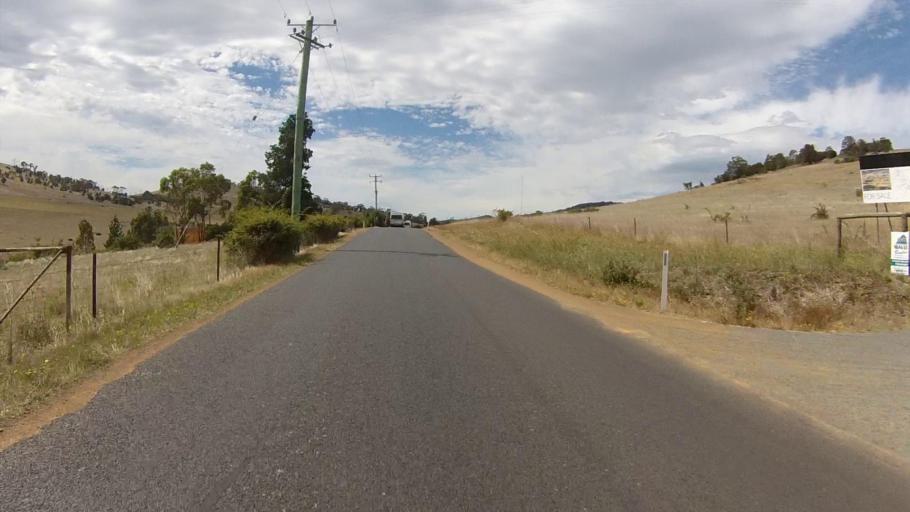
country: AU
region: Tasmania
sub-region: Brighton
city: Old Beach
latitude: -42.7015
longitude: 147.3082
